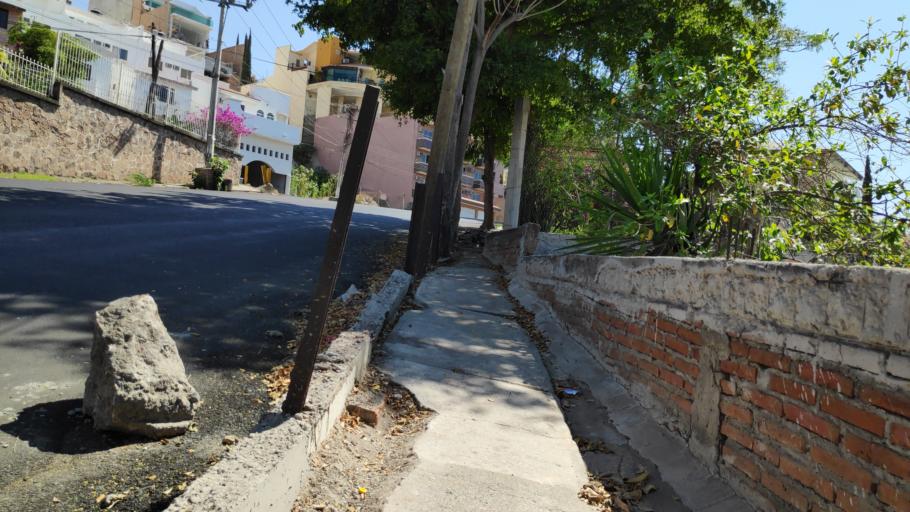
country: MX
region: Sinaloa
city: Culiacan
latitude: 24.7851
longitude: -107.4009
